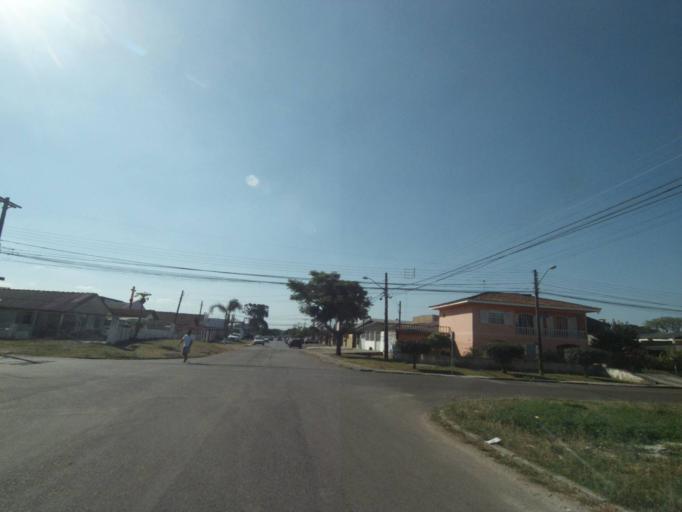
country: BR
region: Parana
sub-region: Sao Jose Dos Pinhais
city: Sao Jose dos Pinhais
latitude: -25.4876
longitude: -49.2361
